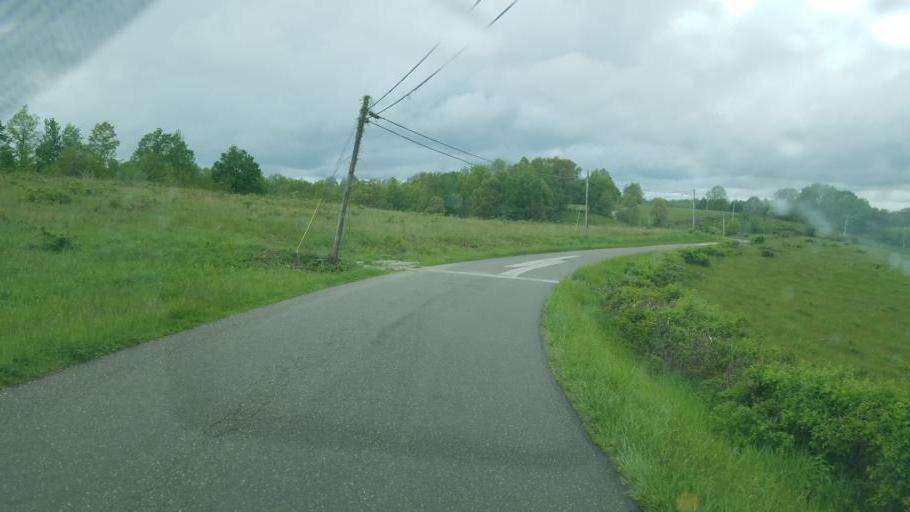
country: US
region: Ohio
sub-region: Tuscarawas County
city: Rockford
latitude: 40.4017
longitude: -81.1952
